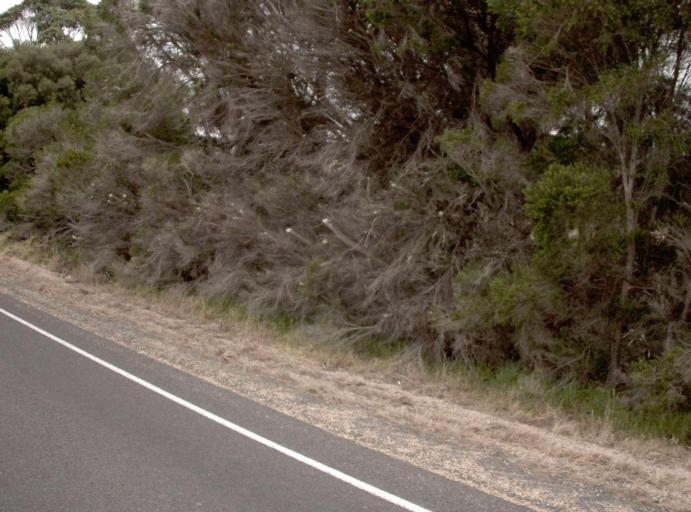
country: AU
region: Victoria
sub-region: Wellington
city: Sale
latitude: -38.0907
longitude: 146.9867
